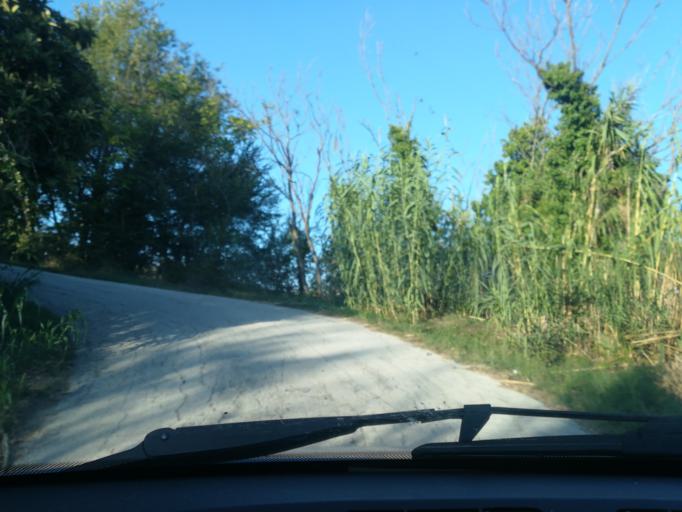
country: IT
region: The Marches
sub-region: Provincia di Macerata
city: Macerata
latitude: 43.2857
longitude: 13.4628
